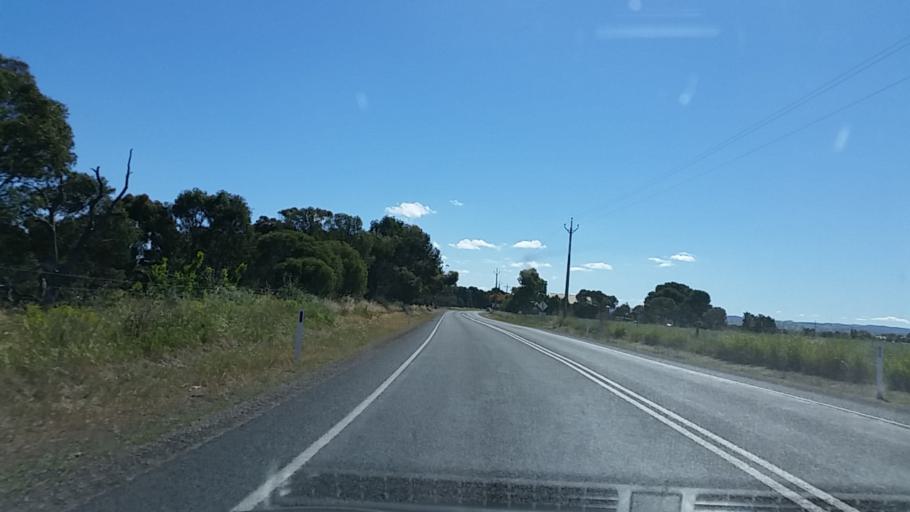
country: AU
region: South Australia
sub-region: Alexandrina
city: Strathalbyn
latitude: -35.2920
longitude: 138.9489
